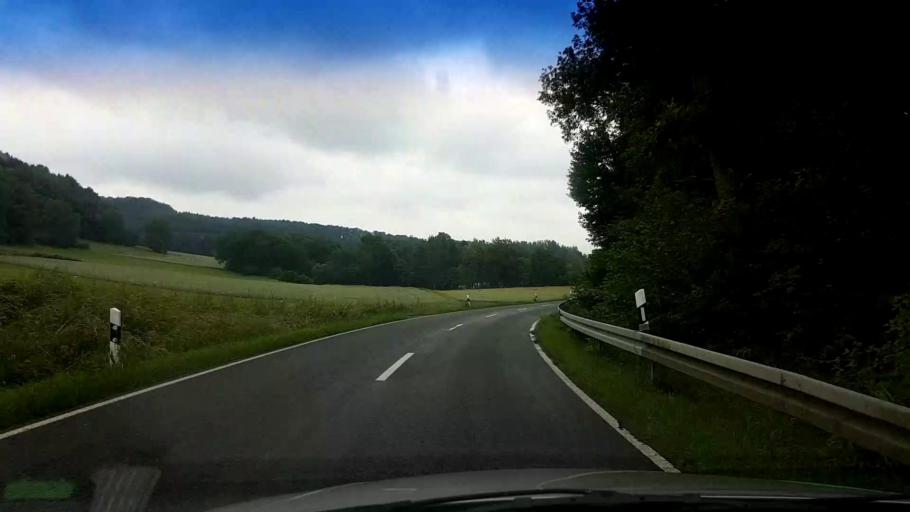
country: DE
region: Bavaria
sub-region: Upper Franconia
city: Weismain
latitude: 50.0727
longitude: 11.2228
